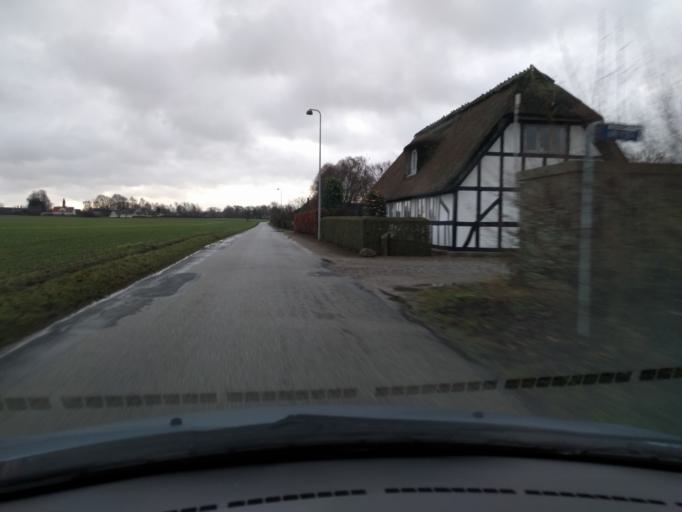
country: DK
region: South Denmark
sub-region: Kerteminde Kommune
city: Langeskov
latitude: 55.3471
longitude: 10.5450
